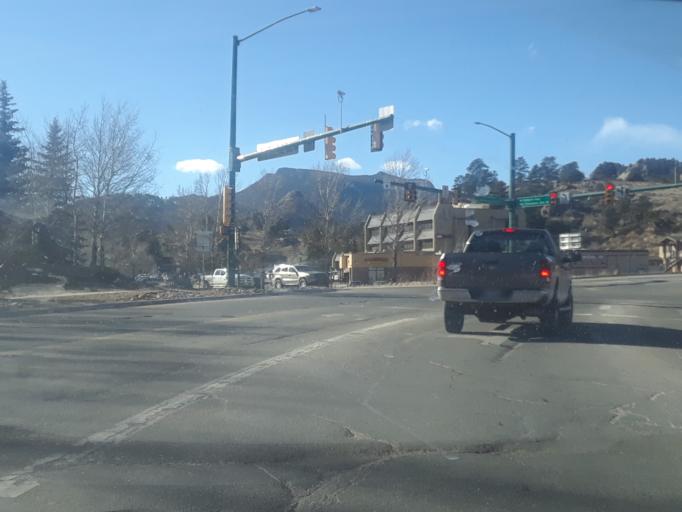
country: US
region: Colorado
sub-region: Larimer County
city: Estes Park
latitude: 40.3778
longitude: -105.5164
